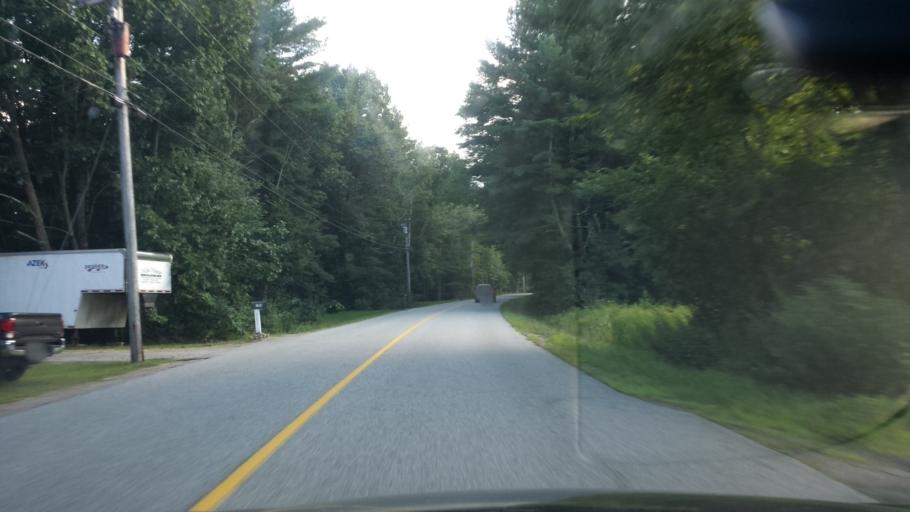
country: US
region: Maine
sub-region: York County
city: Biddeford
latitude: 43.4367
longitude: -70.4473
